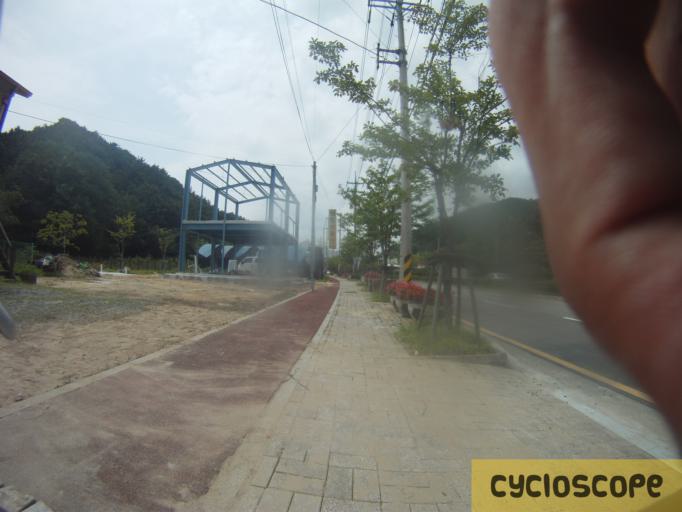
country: KR
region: Busan
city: Kijang
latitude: 35.2608
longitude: 129.2273
